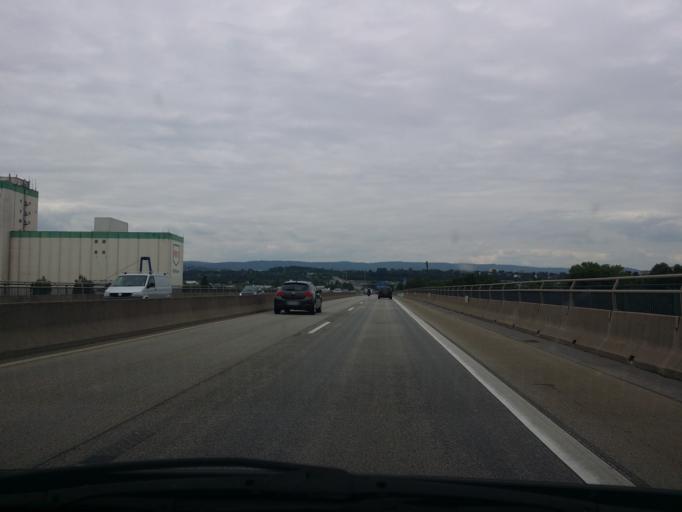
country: DE
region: Rheinland-Pfalz
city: Budenheim
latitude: 50.0376
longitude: 8.2125
